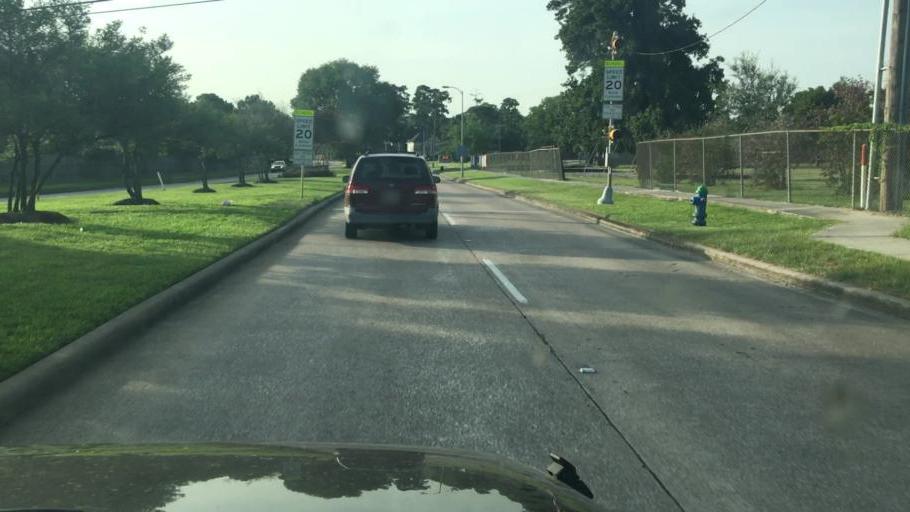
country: US
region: Texas
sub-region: Harris County
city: Atascocita
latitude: 30.0023
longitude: -95.1636
